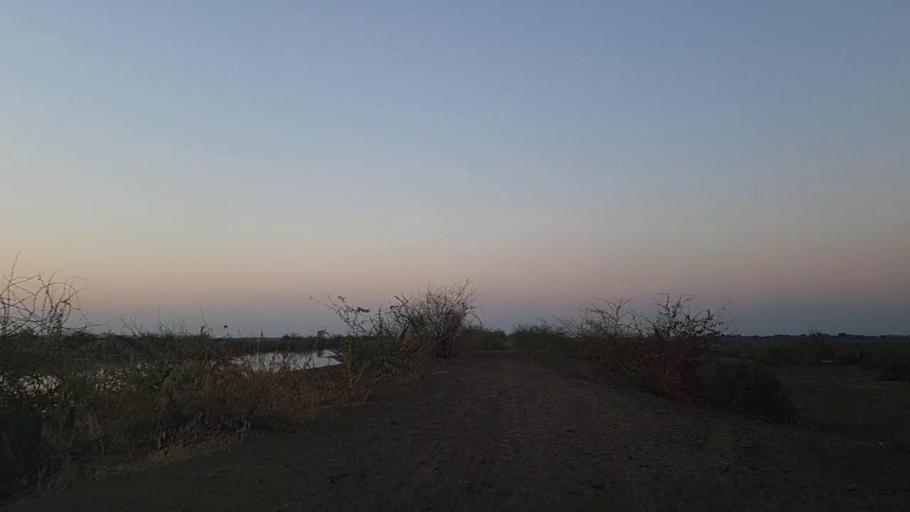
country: PK
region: Sindh
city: Tando Mittha Khan
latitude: 26.0748
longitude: 69.1544
